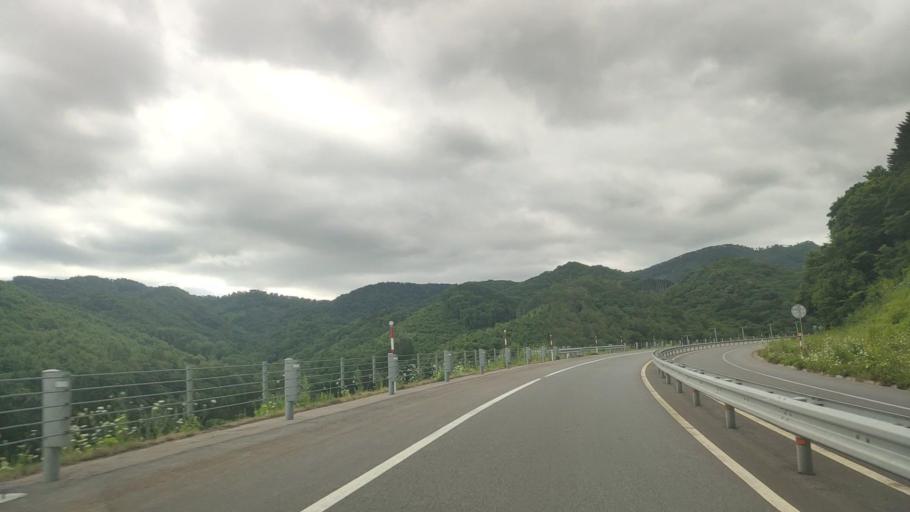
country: JP
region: Hokkaido
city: Niseko Town
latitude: 42.5974
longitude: 140.5781
